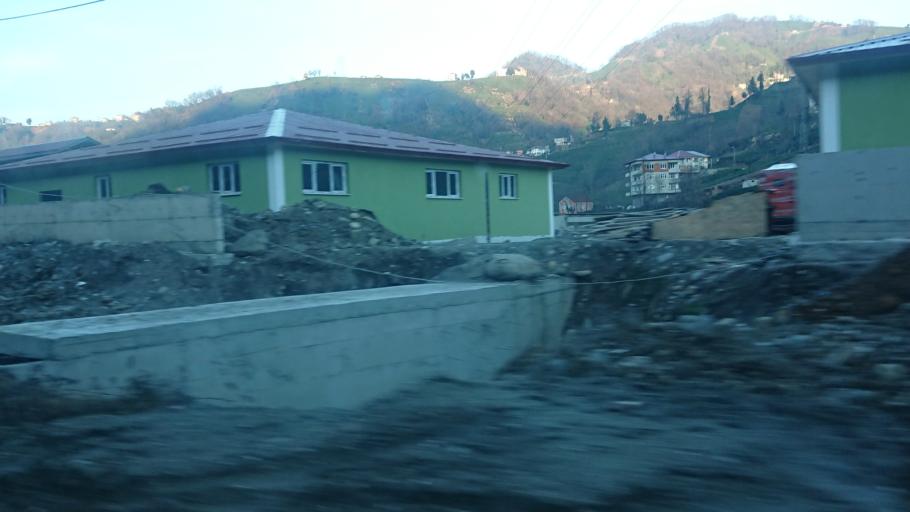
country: TR
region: Rize
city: Gundogdu
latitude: 41.0240
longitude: 40.5768
